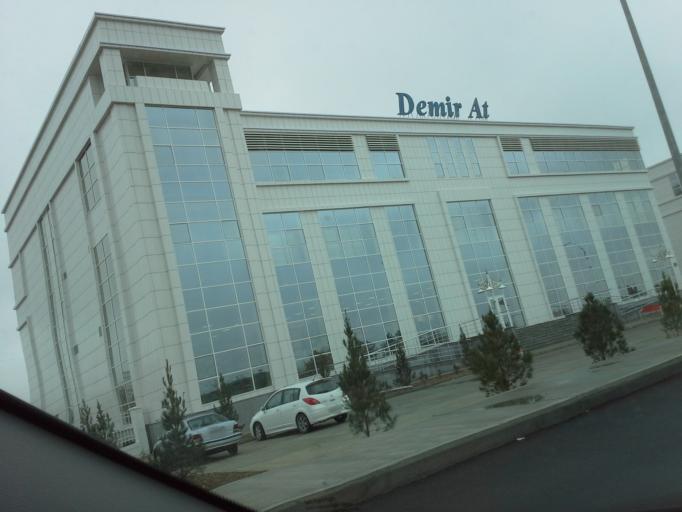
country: TM
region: Ahal
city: Ashgabat
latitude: 37.9532
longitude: 58.4262
